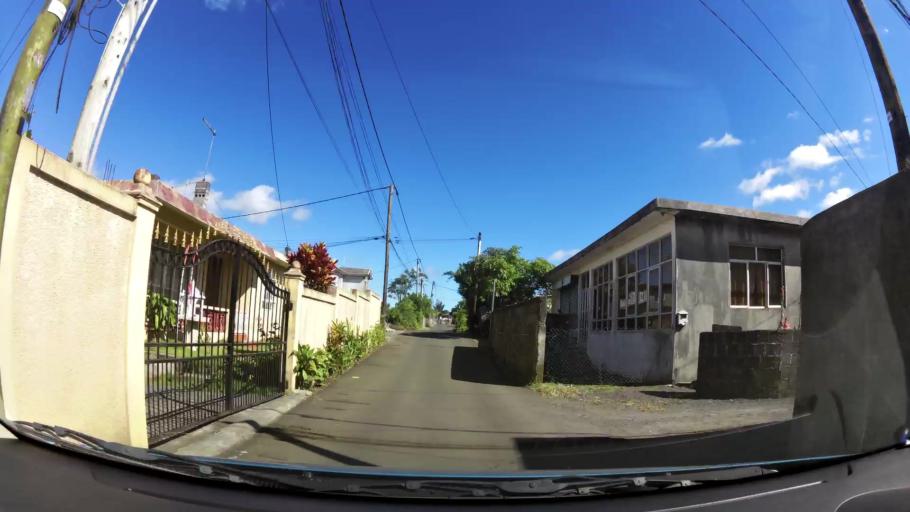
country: MU
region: Plaines Wilhems
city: Vacoas
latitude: -20.3169
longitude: 57.4887
